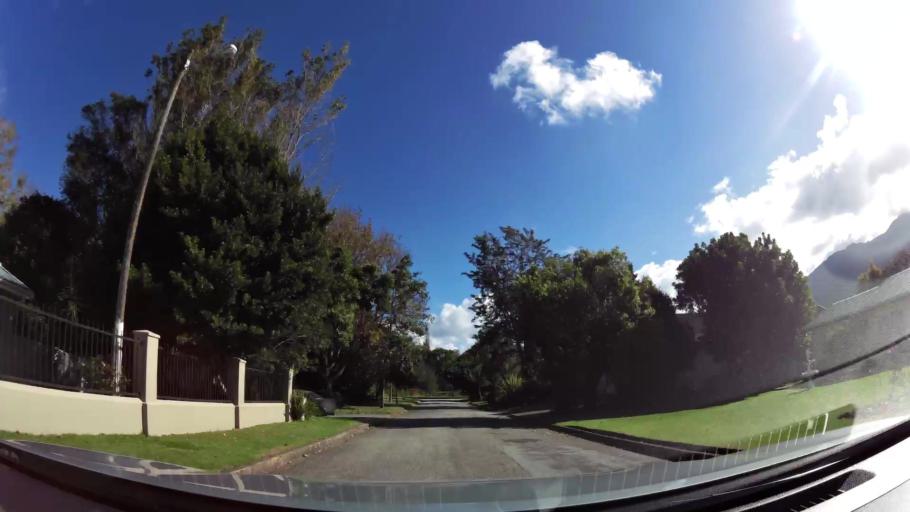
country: ZA
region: Western Cape
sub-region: Eden District Municipality
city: George
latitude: -33.9504
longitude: 22.4577
